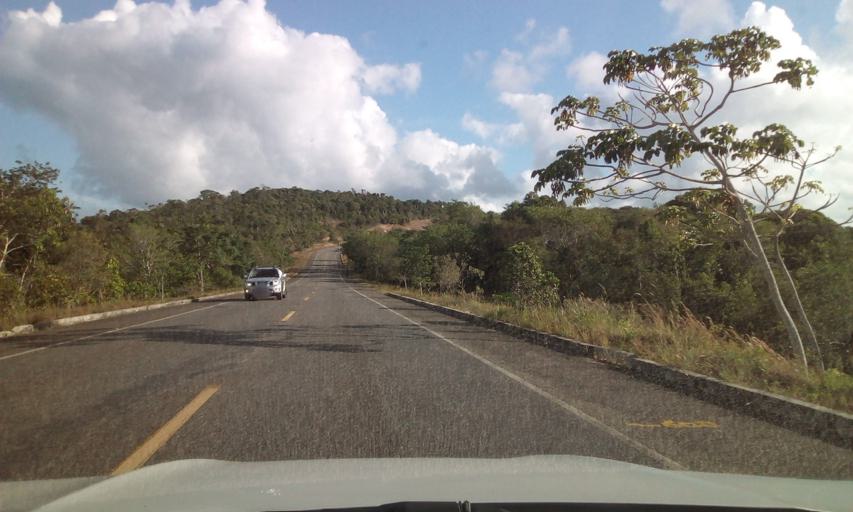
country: BR
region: Bahia
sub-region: Conde
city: Conde
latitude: -12.0883
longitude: -37.7732
